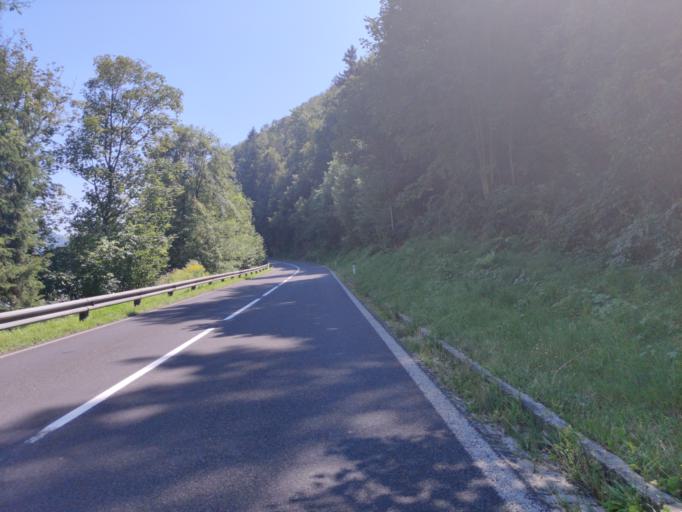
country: AT
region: Upper Austria
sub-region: Politischer Bezirk Rohrbach
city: Pfarrkirchen im Muehlkreis
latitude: 48.4685
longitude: 13.7763
